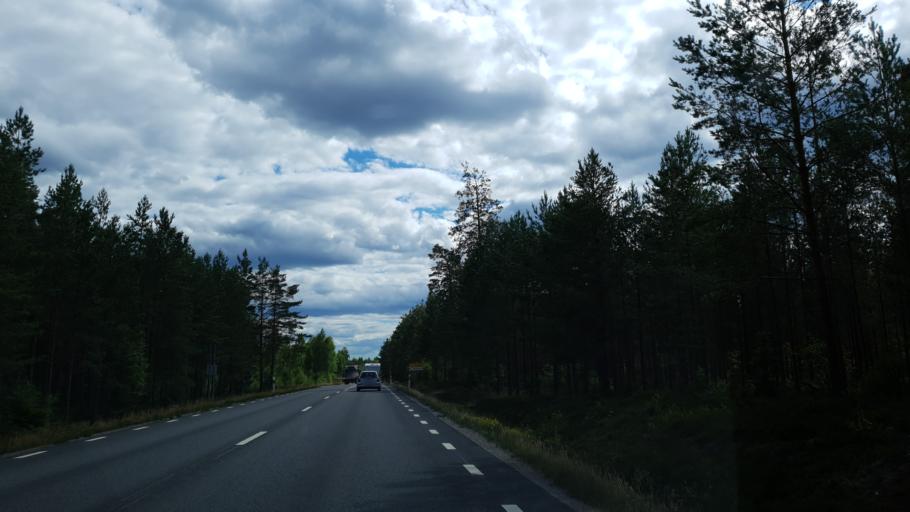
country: SE
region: Kronoberg
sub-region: Lessebo Kommun
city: Lessebo
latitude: 56.8012
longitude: 15.4123
